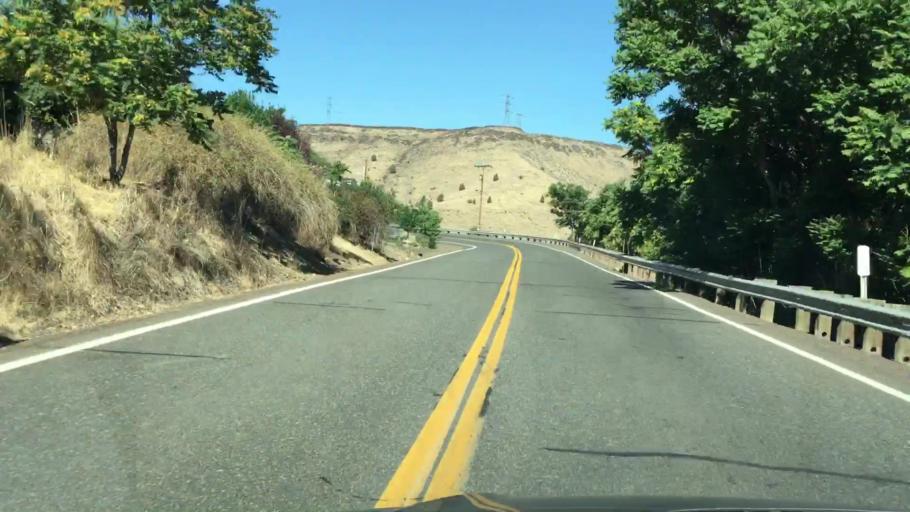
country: US
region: Oregon
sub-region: Wasco County
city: The Dalles
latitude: 45.1774
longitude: -121.0766
